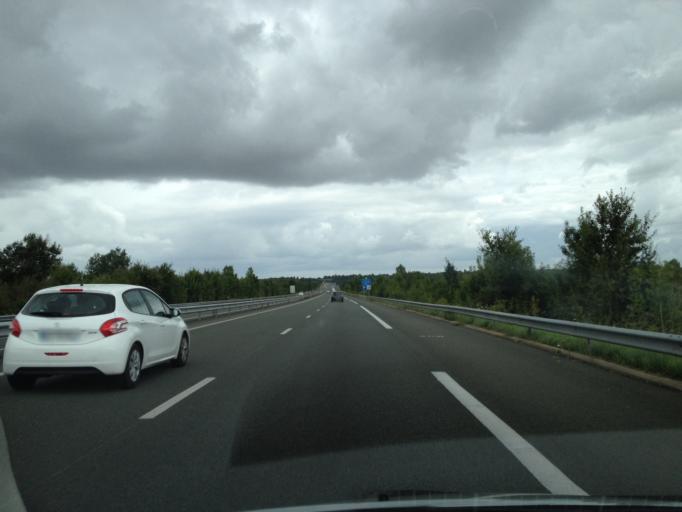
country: FR
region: Pays de la Loire
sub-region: Departement de la Vendee
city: Saint-Martin-des-Noyers
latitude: 46.7540
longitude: -1.1673
